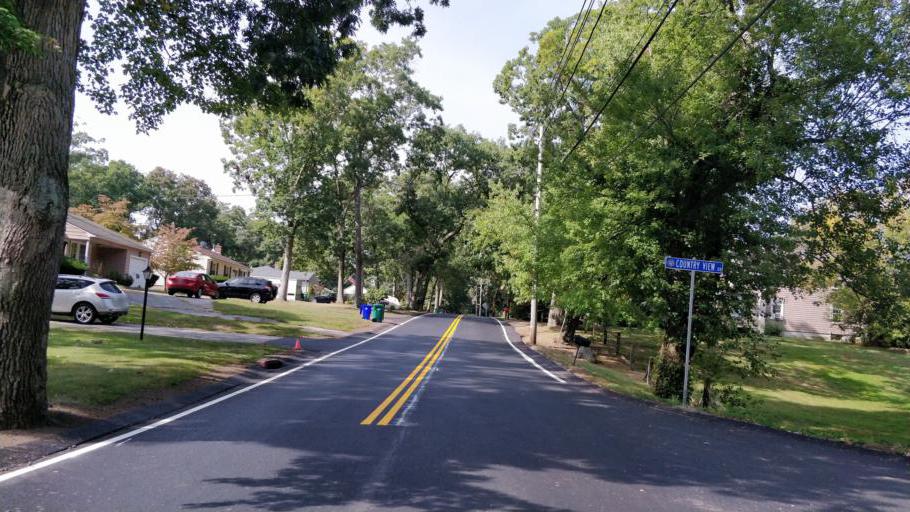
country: US
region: Massachusetts
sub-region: Bristol County
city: North Seekonk
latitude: 41.9043
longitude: -71.3261
